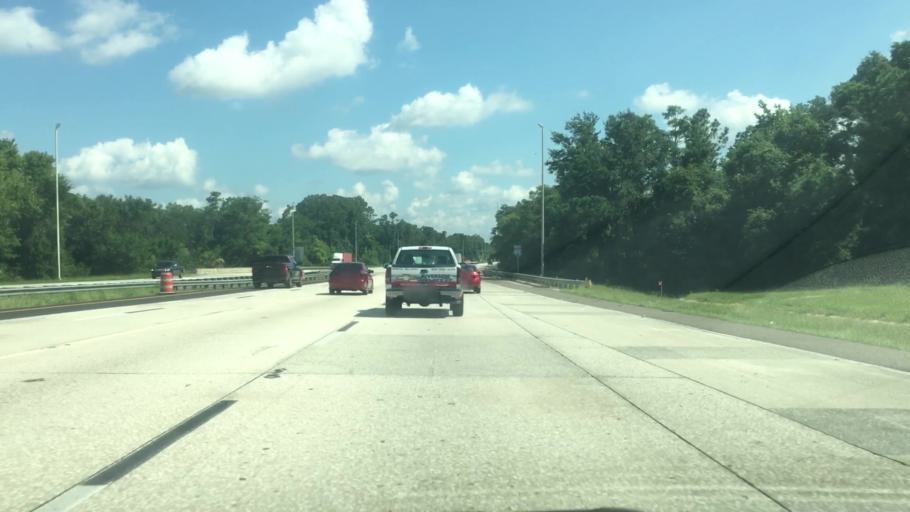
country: US
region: Florida
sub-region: Duval County
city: Jacksonville
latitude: 30.4353
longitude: -81.6557
